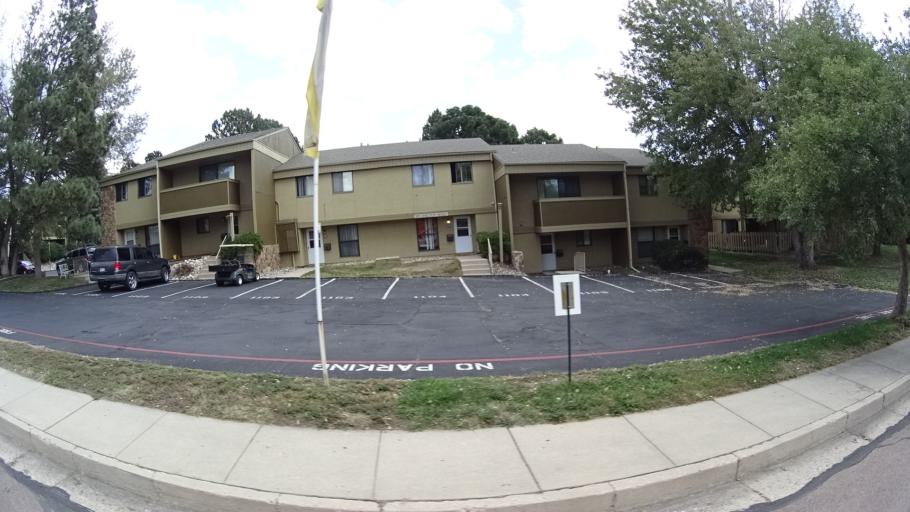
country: US
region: Colorado
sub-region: El Paso County
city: Colorado Springs
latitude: 38.8460
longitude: -104.7665
